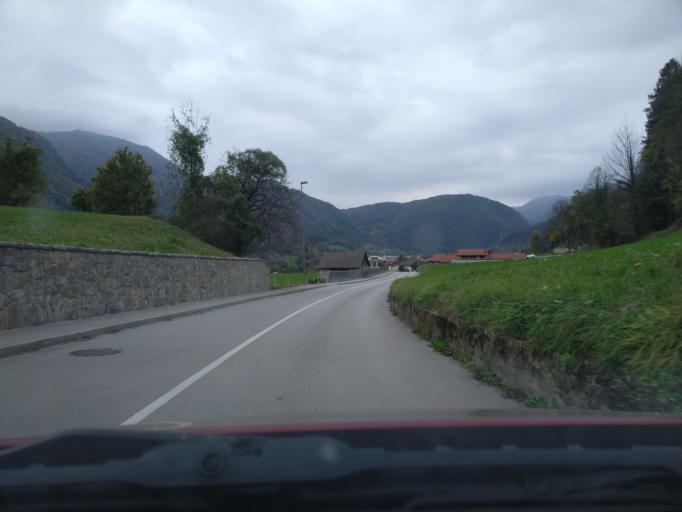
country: SI
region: Tolmin
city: Tolmin
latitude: 46.1921
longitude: 13.7287
